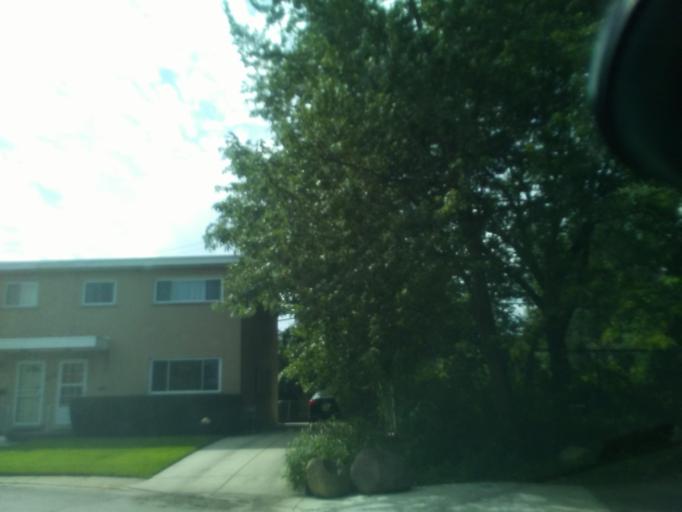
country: US
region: Illinois
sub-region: Cook County
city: Evanston
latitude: 42.0131
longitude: -87.6926
